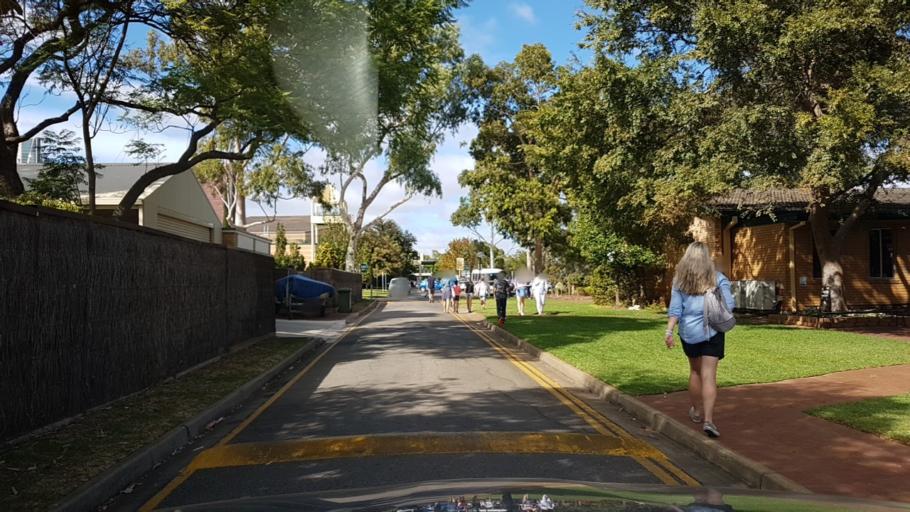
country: AU
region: South Australia
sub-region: Marion
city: Sturt
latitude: -35.0010
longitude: 138.5516
